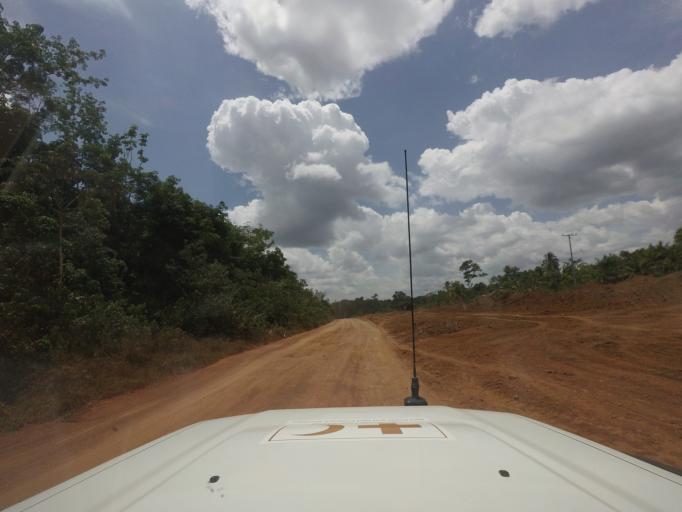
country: LR
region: Nimba
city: Sanniquellie
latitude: 7.2320
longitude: -8.9044
